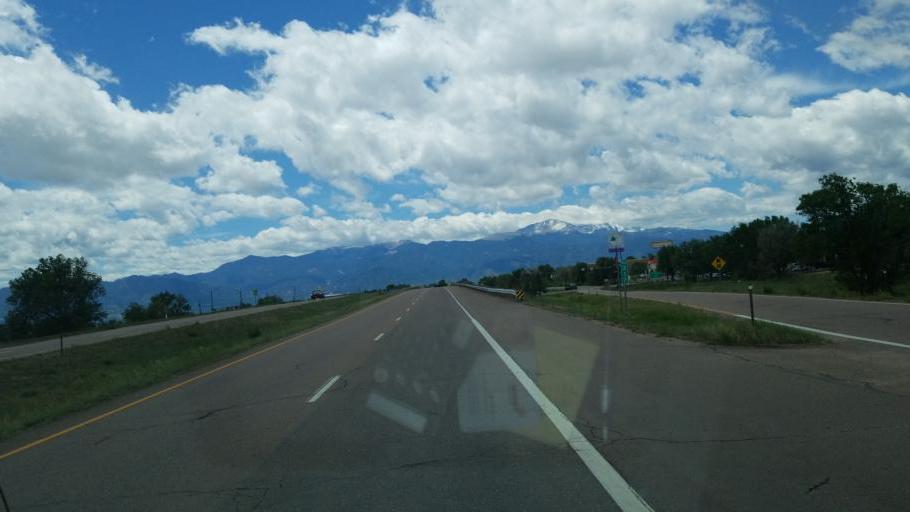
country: US
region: Colorado
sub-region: El Paso County
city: Cimarron Hills
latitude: 38.8399
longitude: -104.6987
